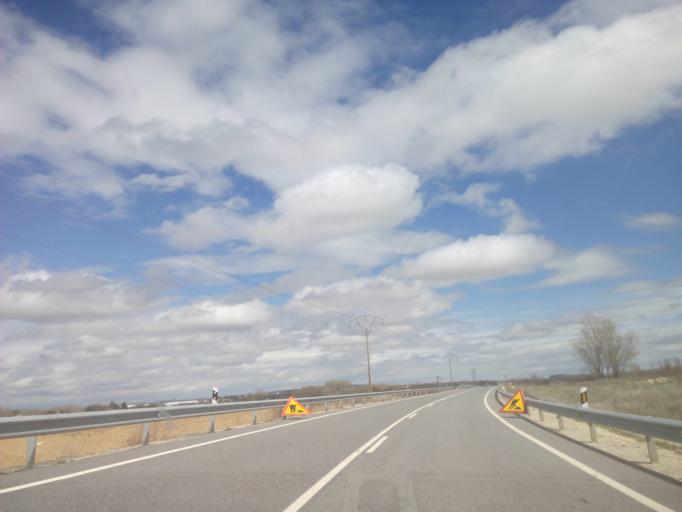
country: ES
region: Castille and Leon
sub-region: Provincia de Salamanca
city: Machacon
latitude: 40.9295
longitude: -5.5030
